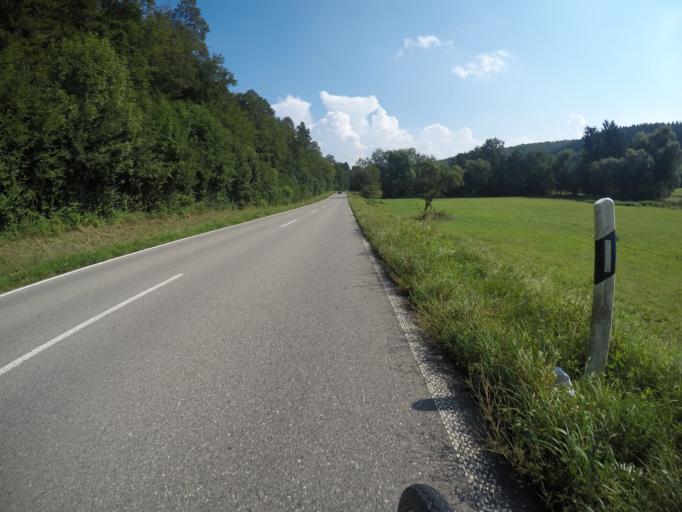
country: DE
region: Baden-Wuerttemberg
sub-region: Regierungsbezirk Stuttgart
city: Filderstadt
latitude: 48.6334
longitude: 9.1906
